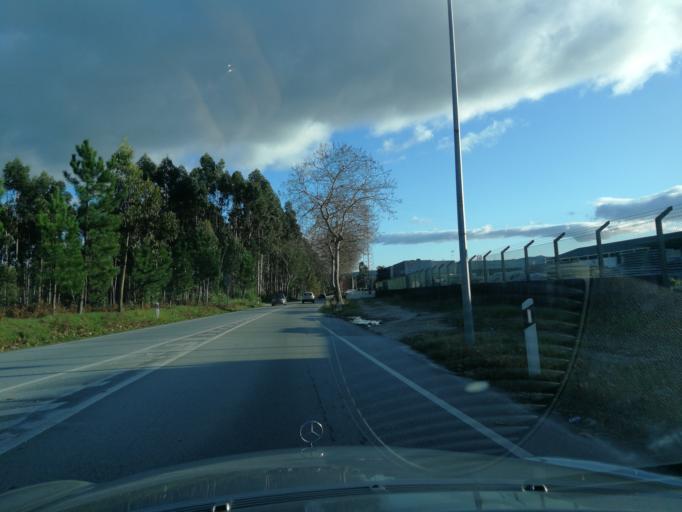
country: PT
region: Viana do Castelo
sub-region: Viana do Castelo
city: Darque
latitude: 41.6326
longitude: -8.7632
